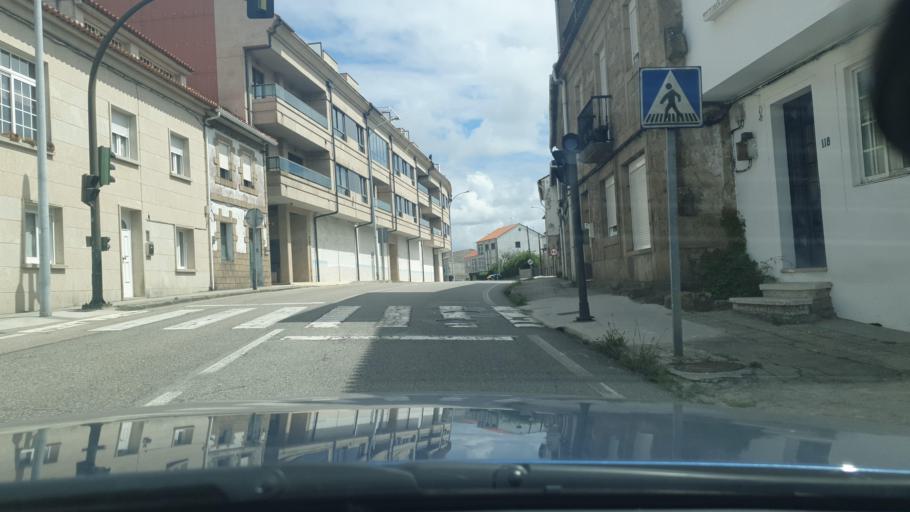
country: ES
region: Galicia
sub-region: Provincia de Pontevedra
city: Cambados
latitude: 42.5082
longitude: -8.8135
